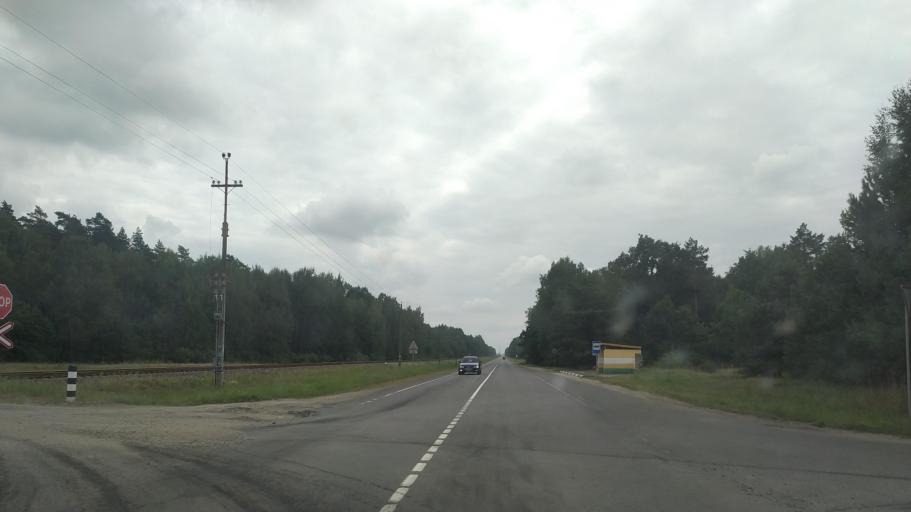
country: BY
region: Brest
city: Byelaazyorsk
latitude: 52.5421
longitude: 25.1369
